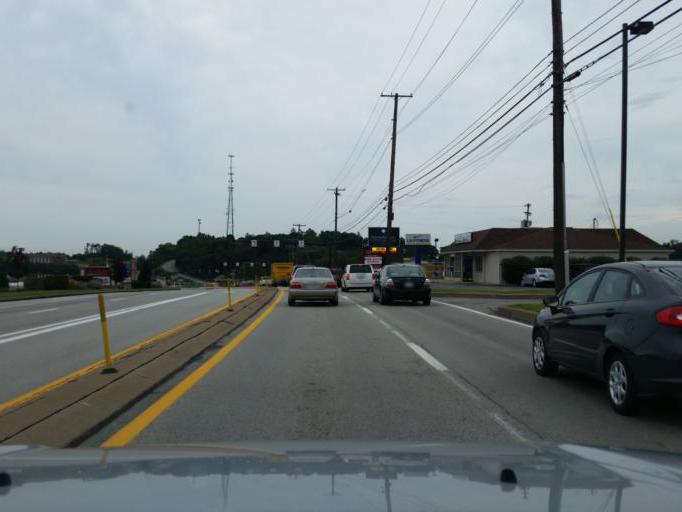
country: US
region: Pennsylvania
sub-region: Westmoreland County
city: Southwest Greensburg
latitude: 40.3048
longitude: -79.5814
